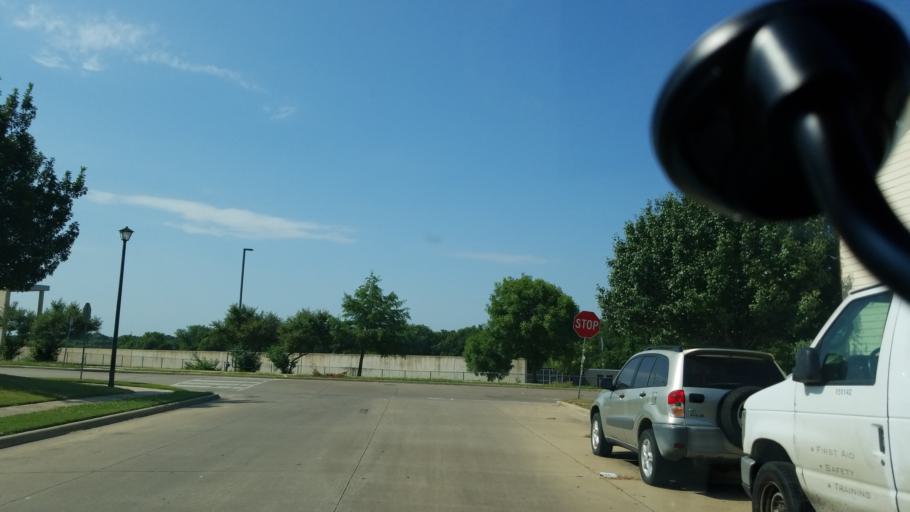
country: US
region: Texas
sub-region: Dallas County
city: Cockrell Hill
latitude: 32.7123
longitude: -96.8692
